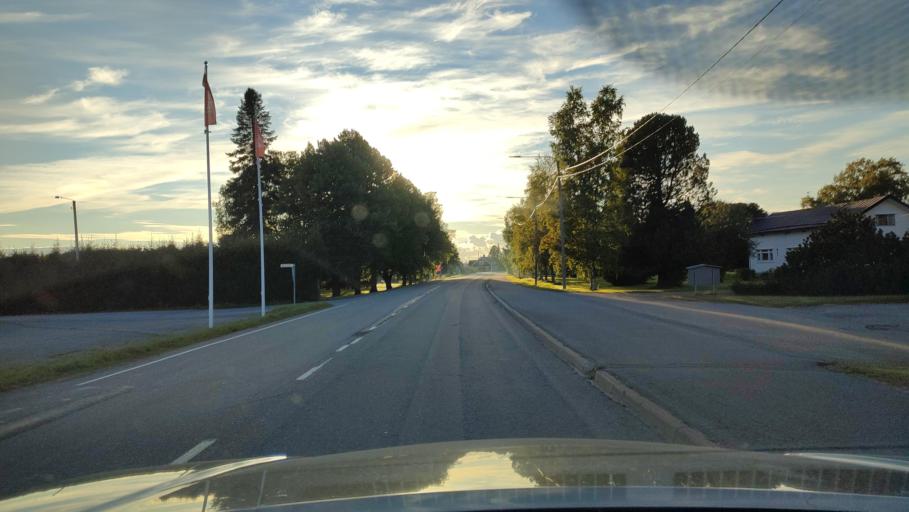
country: FI
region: Ostrobothnia
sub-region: Sydosterbotten
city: Kristinestad
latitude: 62.2548
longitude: 21.5066
